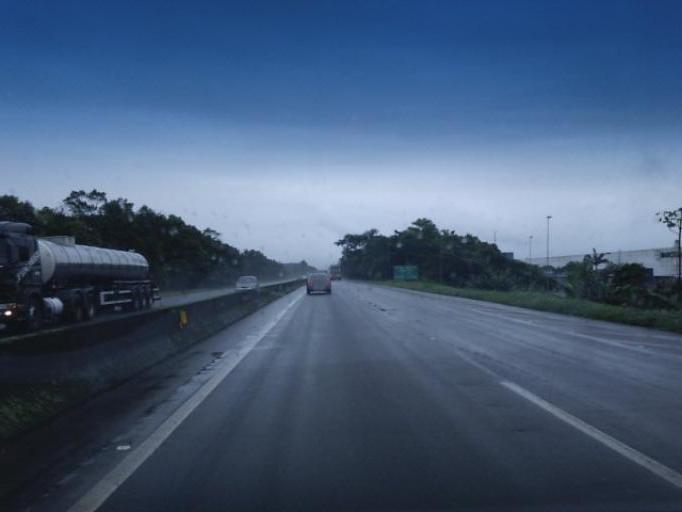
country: BR
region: Santa Catarina
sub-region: Joinville
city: Joinville
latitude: -26.0774
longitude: -48.8614
